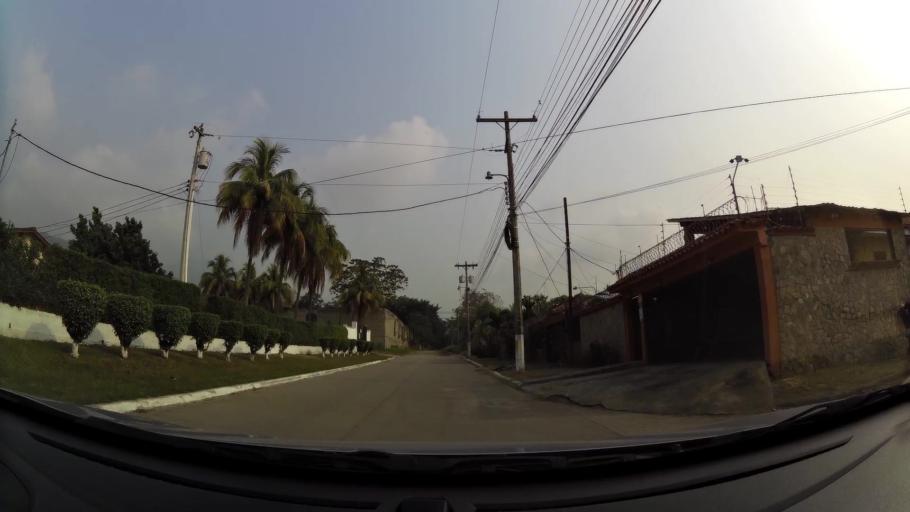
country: HN
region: Cortes
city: Armenta
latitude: 15.4835
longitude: -88.0404
